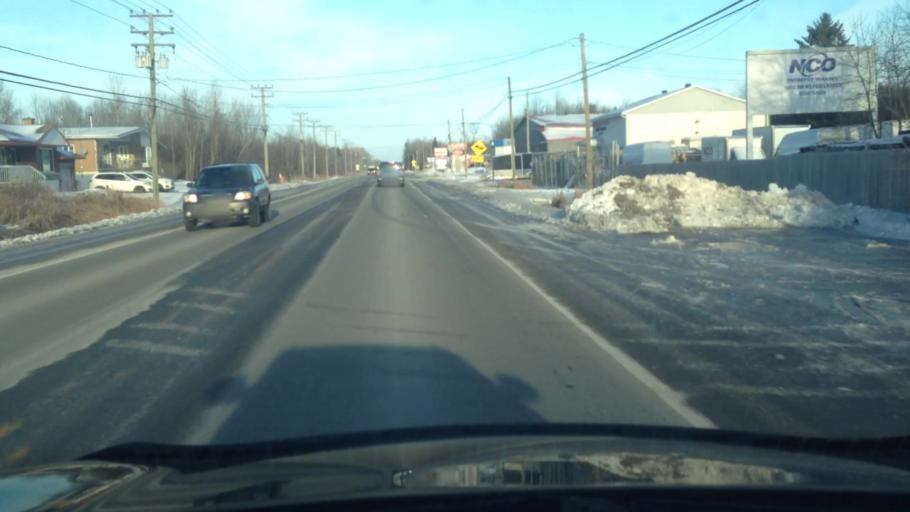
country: CA
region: Quebec
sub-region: Laurentides
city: Saint-Jerome
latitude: 45.7822
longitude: -73.9572
